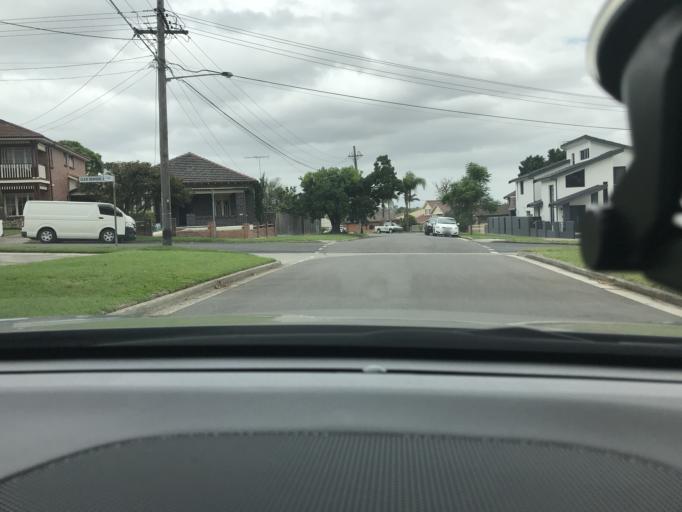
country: AU
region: New South Wales
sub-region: Canada Bay
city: Wareemba
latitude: -33.8532
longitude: 151.1272
